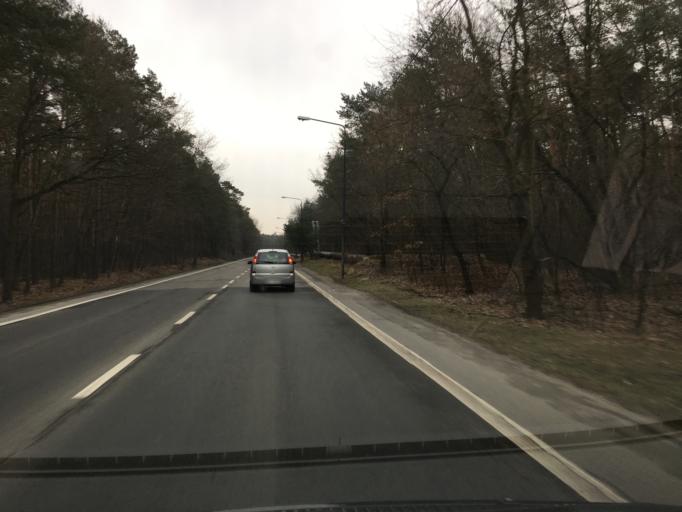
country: PL
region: Opole Voivodeship
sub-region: Powiat kedzierzynsko-kozielski
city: Kedzierzyn-Kozle
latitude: 50.3407
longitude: 18.2267
